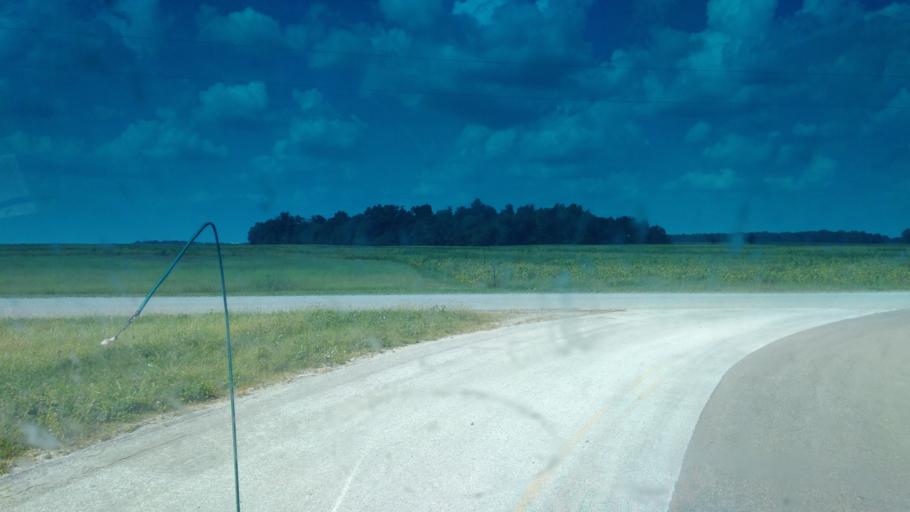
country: US
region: Ohio
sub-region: Hardin County
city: Kenton
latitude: 40.6416
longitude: -83.6827
